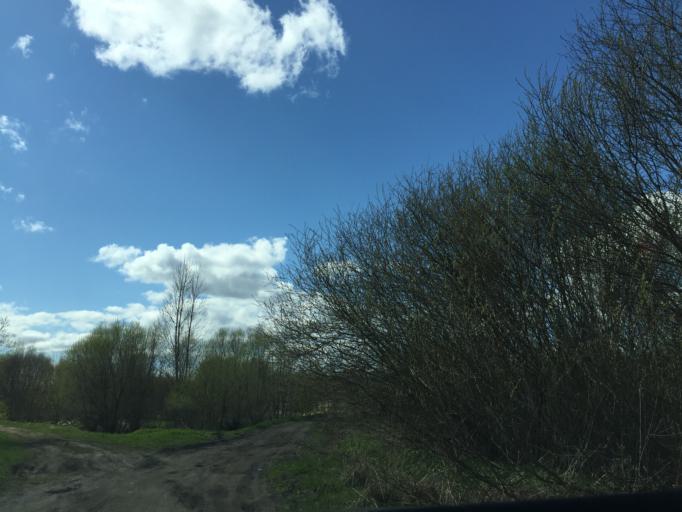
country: LV
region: Rezekne
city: Rezekne
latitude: 56.6982
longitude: 27.2290
